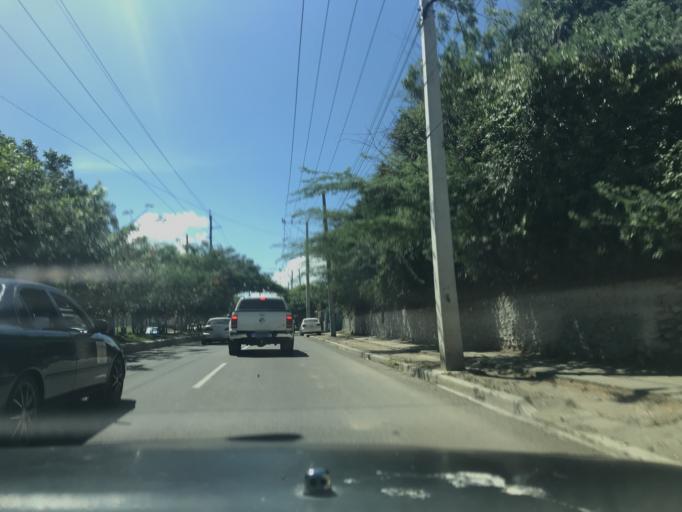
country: DO
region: Santiago
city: Santiago de los Caballeros
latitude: 19.4423
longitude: -70.7360
